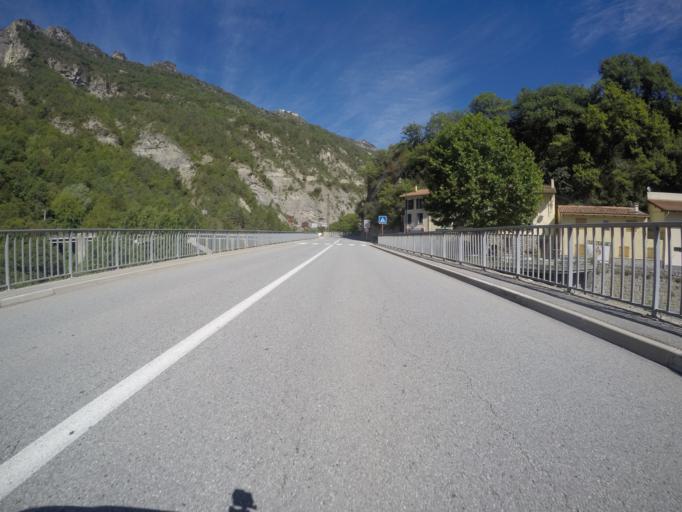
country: FR
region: Provence-Alpes-Cote d'Azur
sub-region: Departement des Alpes-Maritimes
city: Gilette
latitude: 43.9747
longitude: 7.1403
